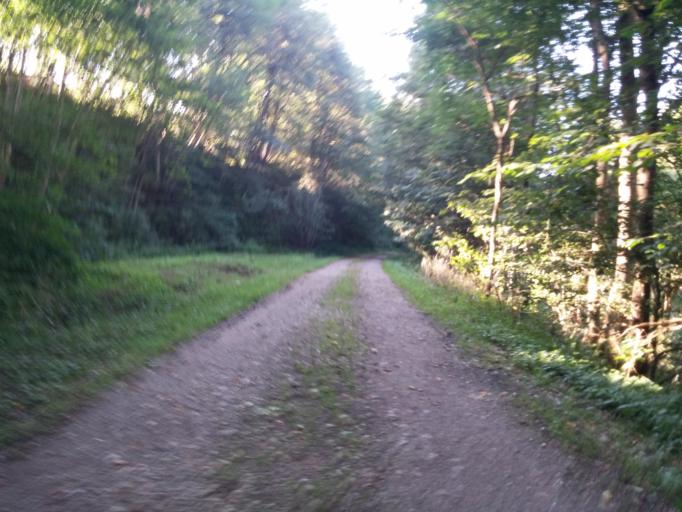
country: DE
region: Bavaria
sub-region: Swabia
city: Lautrach
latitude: 47.8954
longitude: 10.1214
